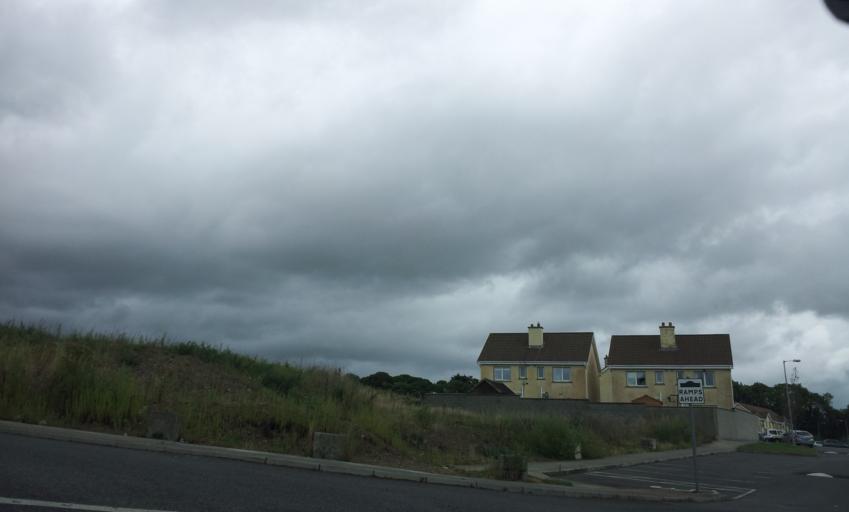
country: IE
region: Munster
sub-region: Waterford
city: Waterford
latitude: 52.2725
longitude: -7.0896
